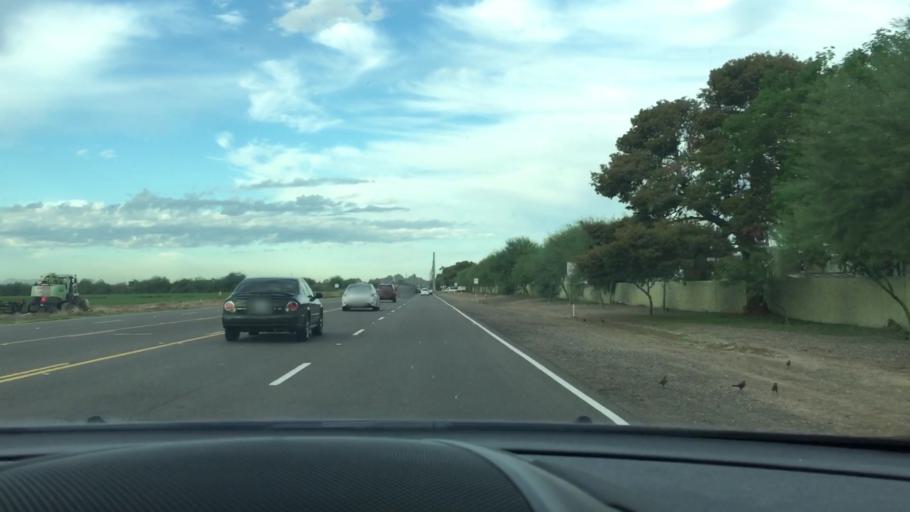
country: US
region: Arizona
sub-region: Maricopa County
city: Tempe
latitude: 33.4508
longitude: -111.8952
